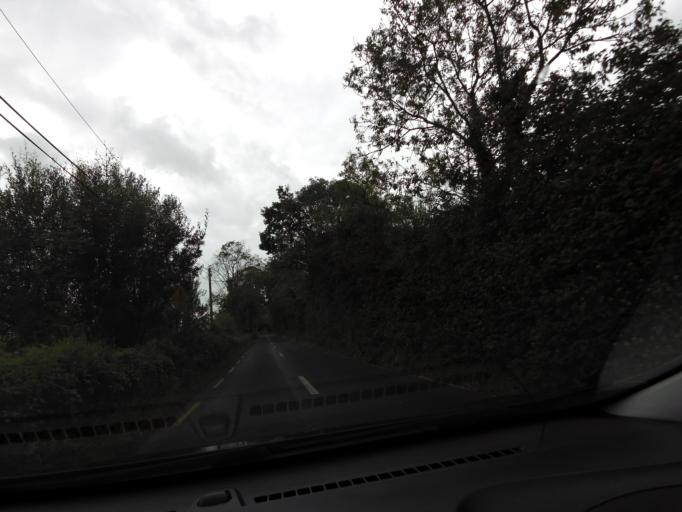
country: IE
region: Connaught
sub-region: County Galway
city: Loughrea
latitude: 53.2848
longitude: -8.6030
